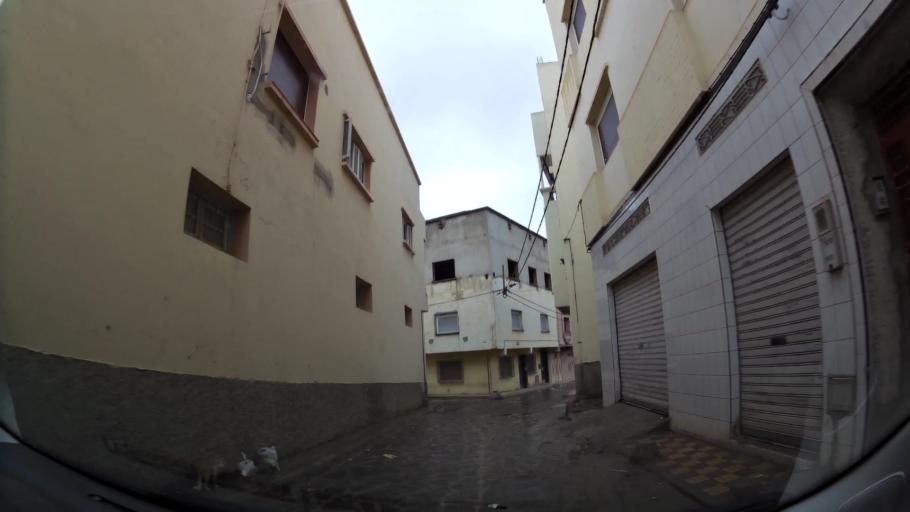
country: MA
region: Oriental
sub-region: Nador
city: Nador
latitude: 35.1751
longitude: -2.9375
